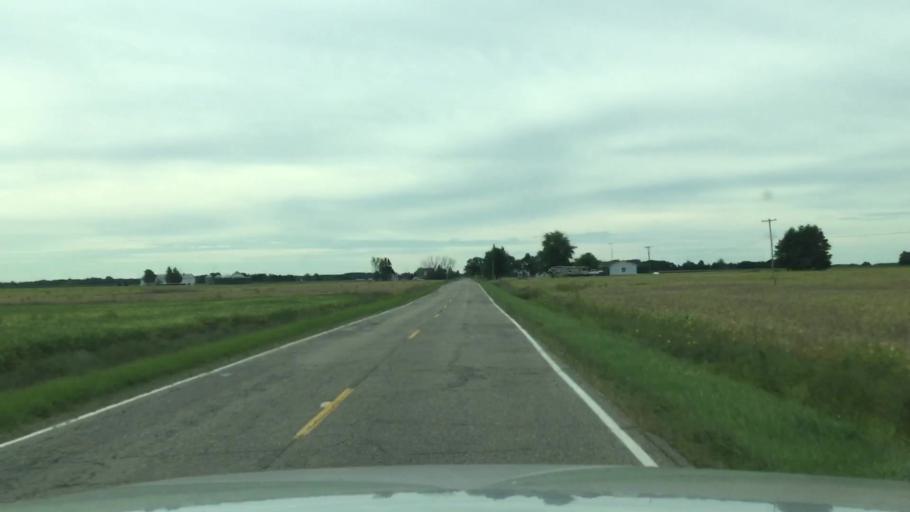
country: US
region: Michigan
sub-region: Genesee County
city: Montrose
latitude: 43.0937
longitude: -83.9878
